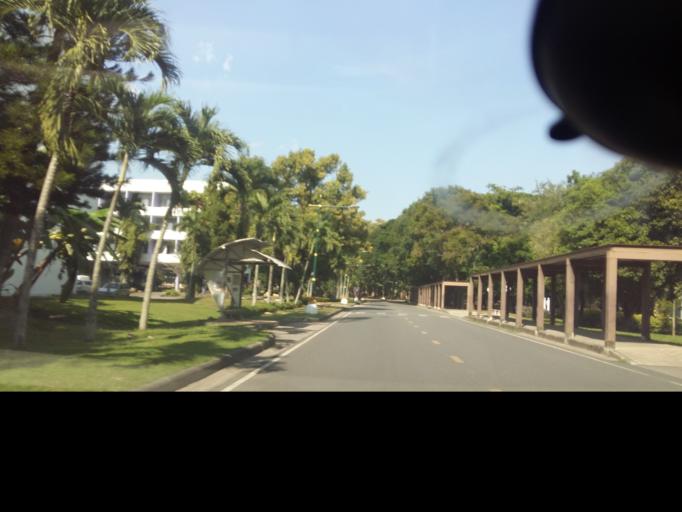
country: TH
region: Chiang Mai
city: Chiang Mai
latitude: 18.7976
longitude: 98.9513
